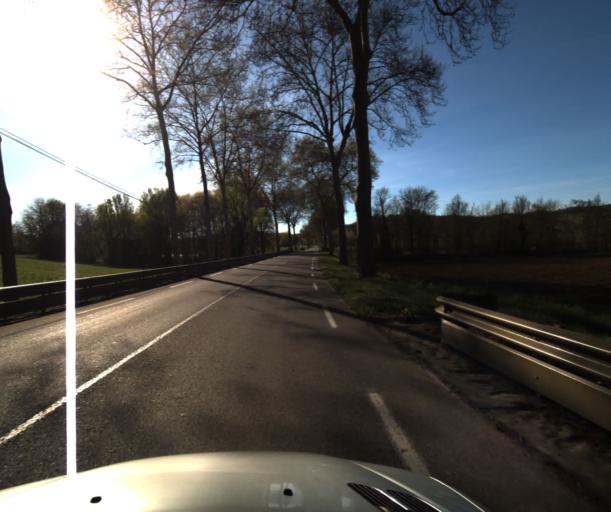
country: FR
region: Midi-Pyrenees
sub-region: Departement du Tarn-et-Garonne
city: Lafrancaise
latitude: 44.1275
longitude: 1.1666
